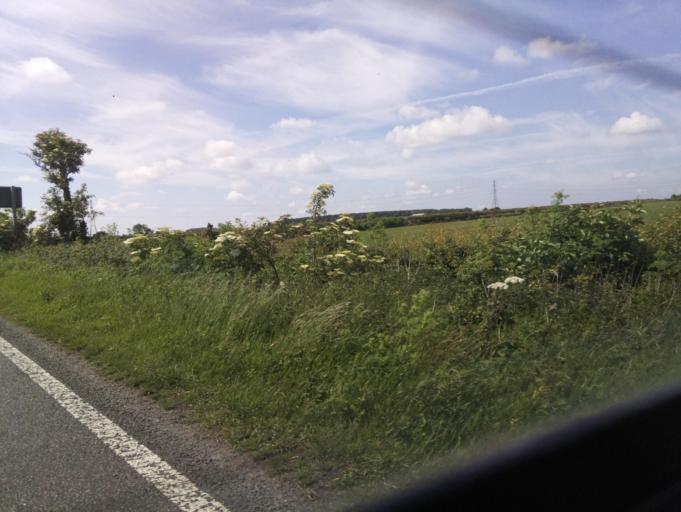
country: GB
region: England
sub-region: Lincolnshire
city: Burton
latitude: 53.2808
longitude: -0.5402
